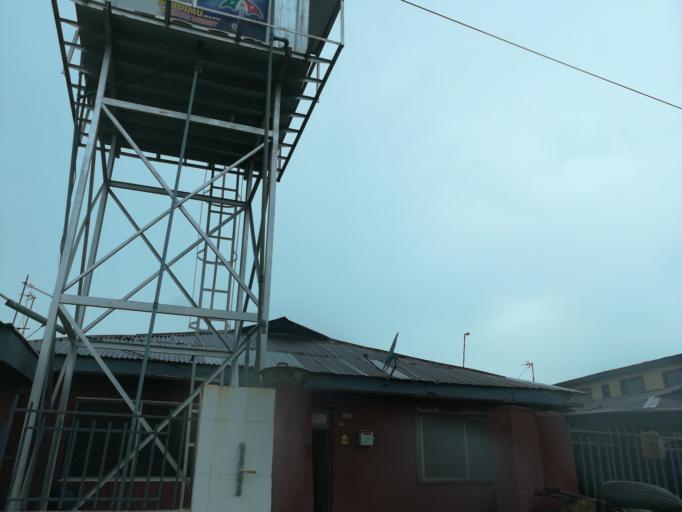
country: NG
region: Lagos
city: Oshodi
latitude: 6.5578
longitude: 3.3418
